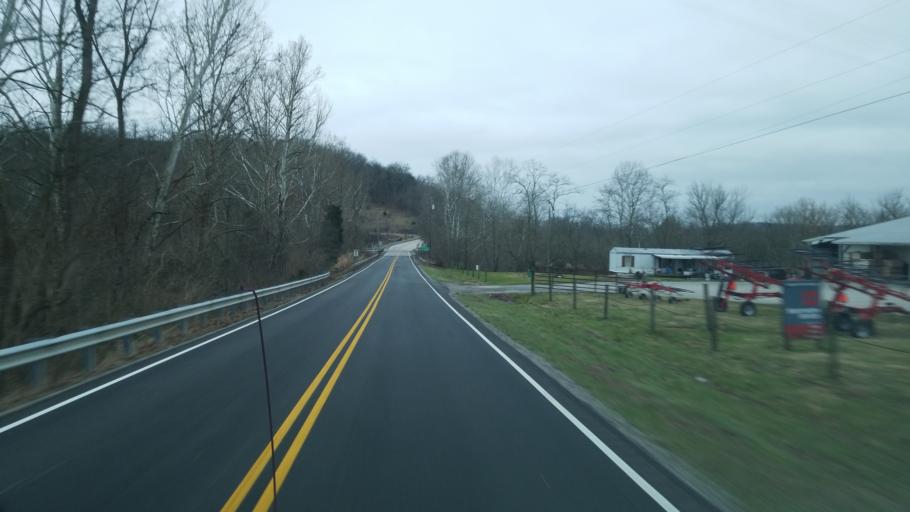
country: US
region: Kentucky
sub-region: Bracken County
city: Augusta
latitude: 38.7716
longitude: -83.9893
